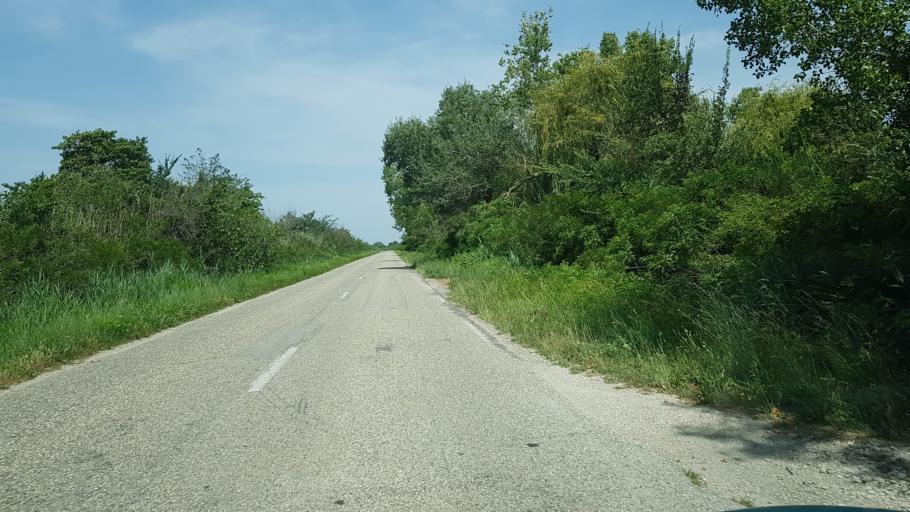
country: FR
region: Languedoc-Roussillon
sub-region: Departement du Gard
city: Saint-Gilles
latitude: 43.5854
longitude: 4.4992
